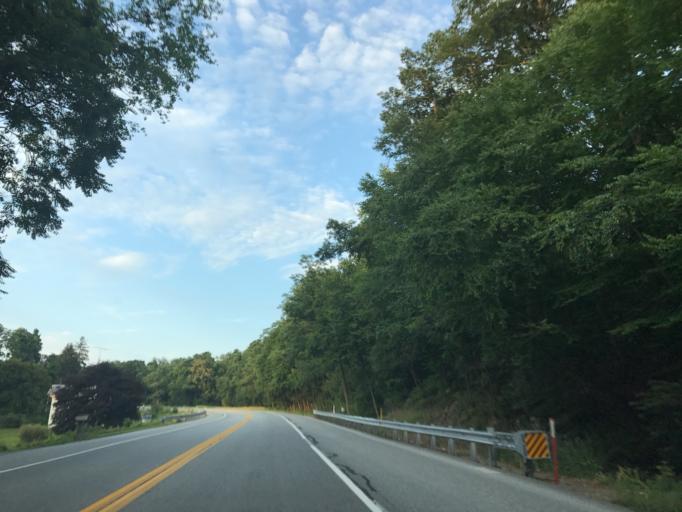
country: US
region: Pennsylvania
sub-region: York County
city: Susquehanna Trails
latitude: 39.8252
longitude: -76.3141
